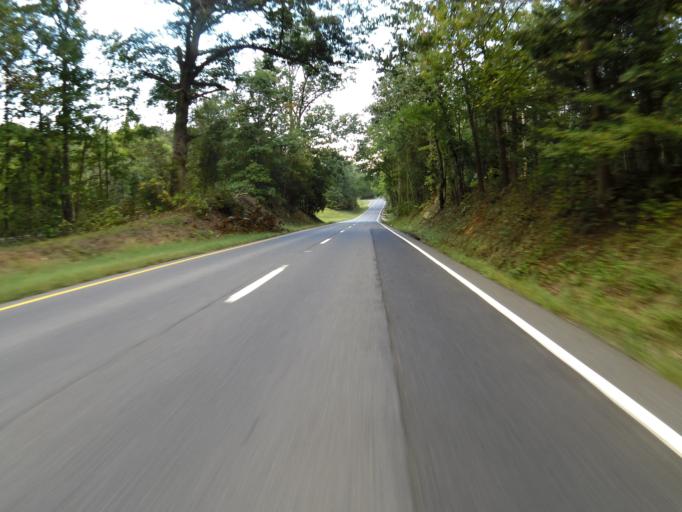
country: US
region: Virginia
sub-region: Fauquier County
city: Warrenton
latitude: 38.6736
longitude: -77.9490
